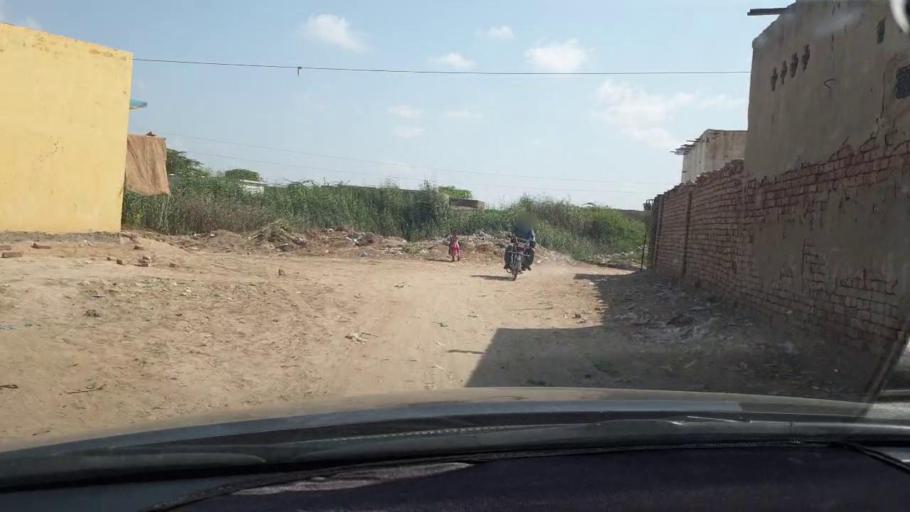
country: PK
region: Sindh
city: Naukot
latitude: 24.8744
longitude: 69.2590
